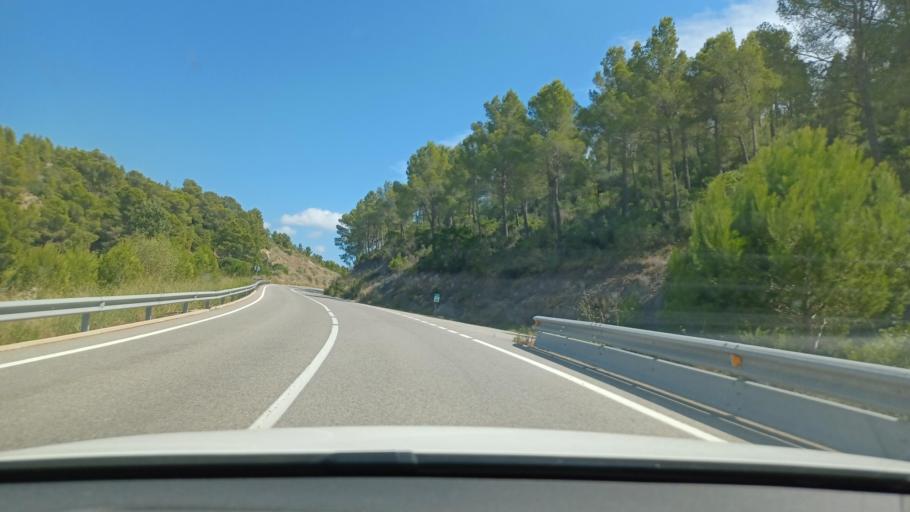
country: ES
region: Catalonia
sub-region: Provincia de Tarragona
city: Tivenys
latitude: 40.9416
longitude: 0.4603
